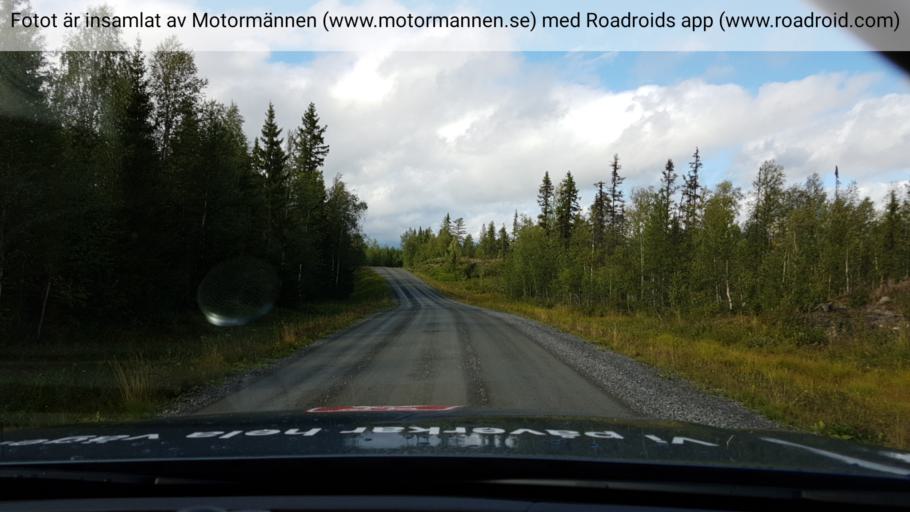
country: SE
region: Jaemtland
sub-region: Krokoms Kommun
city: Krokom
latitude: 63.7235
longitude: 14.5142
